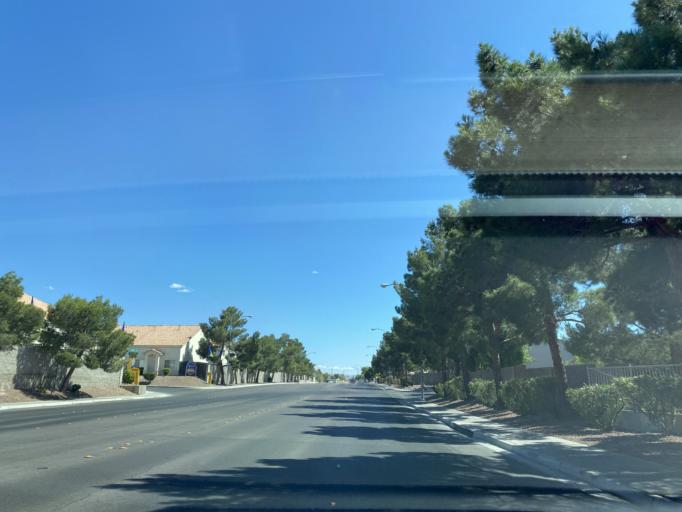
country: US
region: Nevada
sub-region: Clark County
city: Spring Valley
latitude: 36.0915
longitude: -115.2167
